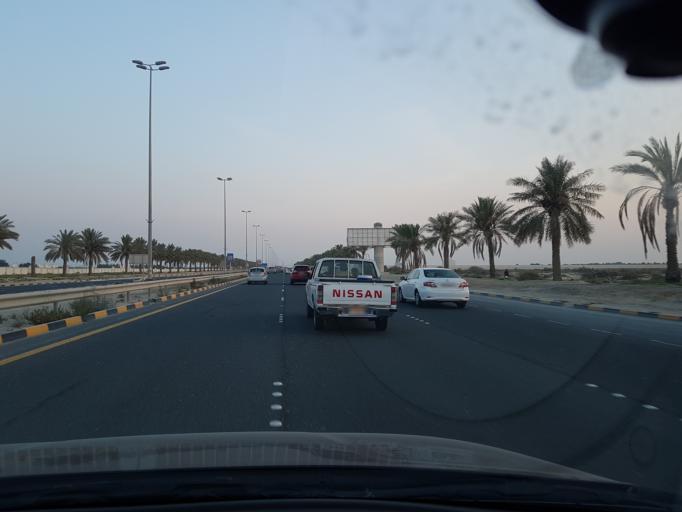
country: BH
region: Central Governorate
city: Dar Kulayb
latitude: 26.0470
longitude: 50.4998
